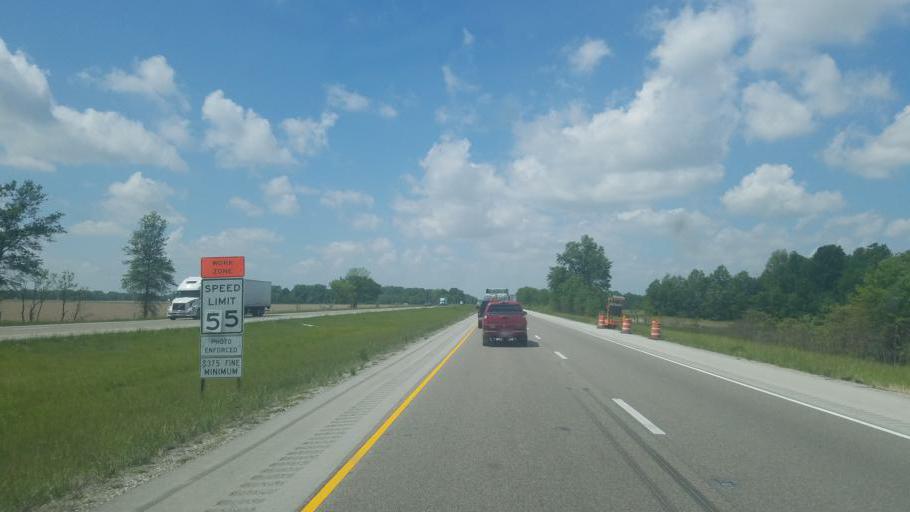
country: US
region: Illinois
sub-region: Cumberland County
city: Toledo
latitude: 39.2269
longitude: -88.2248
